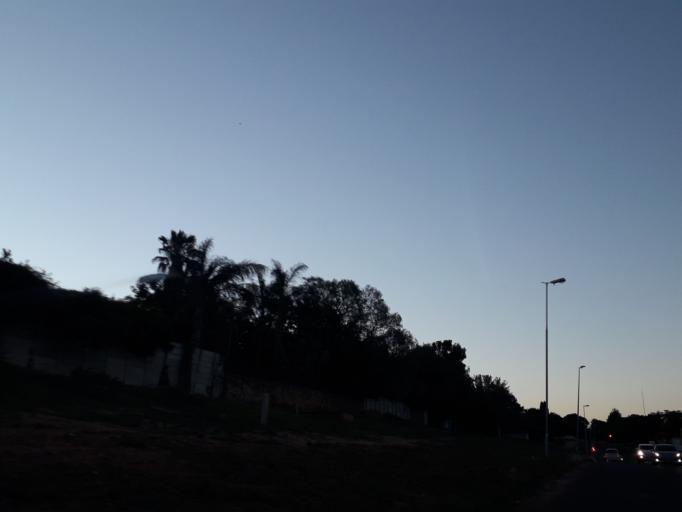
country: ZA
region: Gauteng
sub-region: City of Johannesburg Metropolitan Municipality
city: Roodepoort
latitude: -26.1139
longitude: 27.9324
